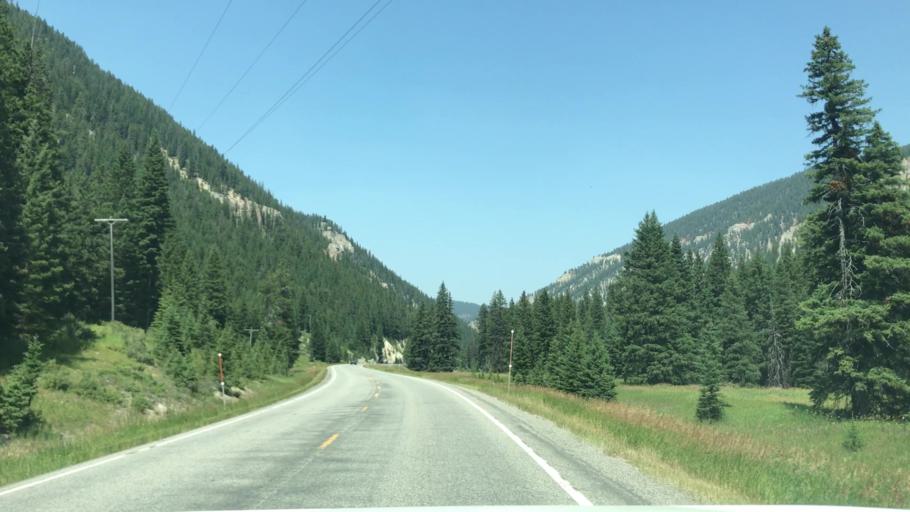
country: US
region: Montana
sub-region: Gallatin County
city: Big Sky
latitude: 45.1252
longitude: -111.2307
